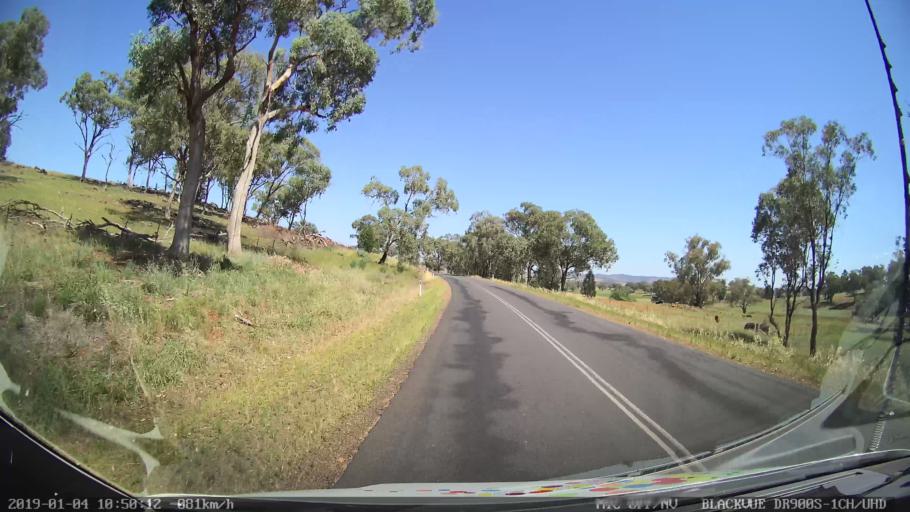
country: AU
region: New South Wales
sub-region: Cabonne
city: Molong
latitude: -33.2428
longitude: 148.6977
